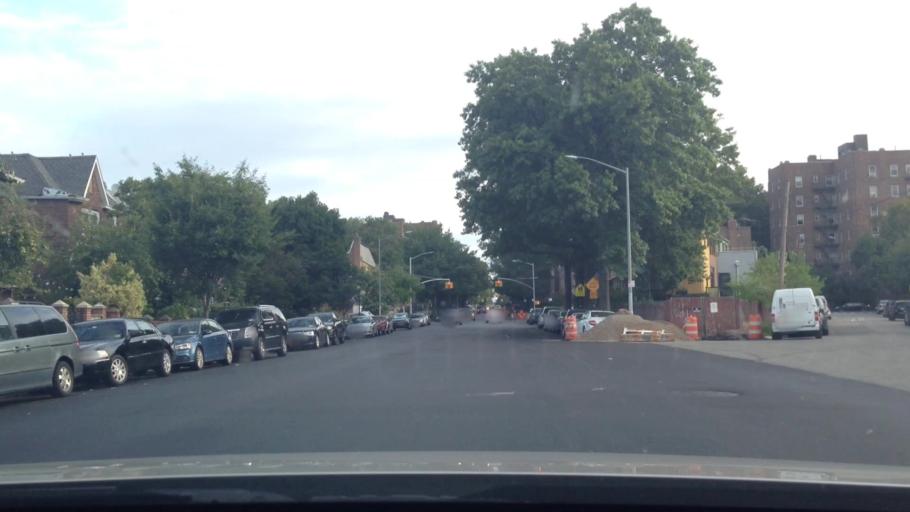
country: US
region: New York
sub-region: Queens County
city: Long Island City
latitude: 40.7366
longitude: -73.9228
